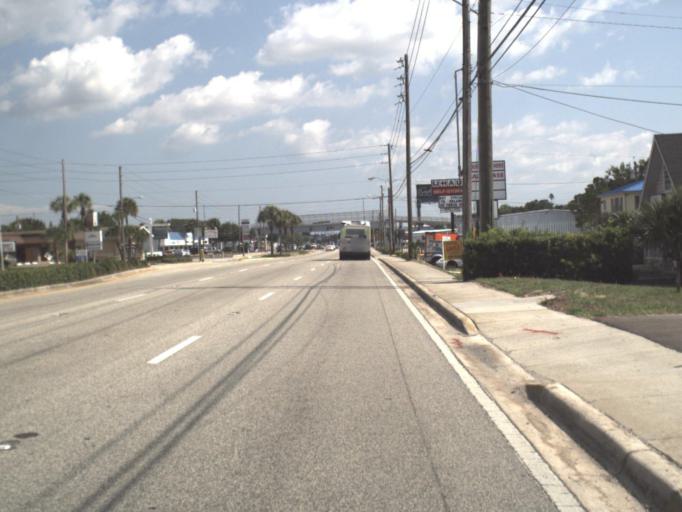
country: US
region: Florida
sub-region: Pinellas County
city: Seminole
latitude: 27.8295
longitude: -82.7869
